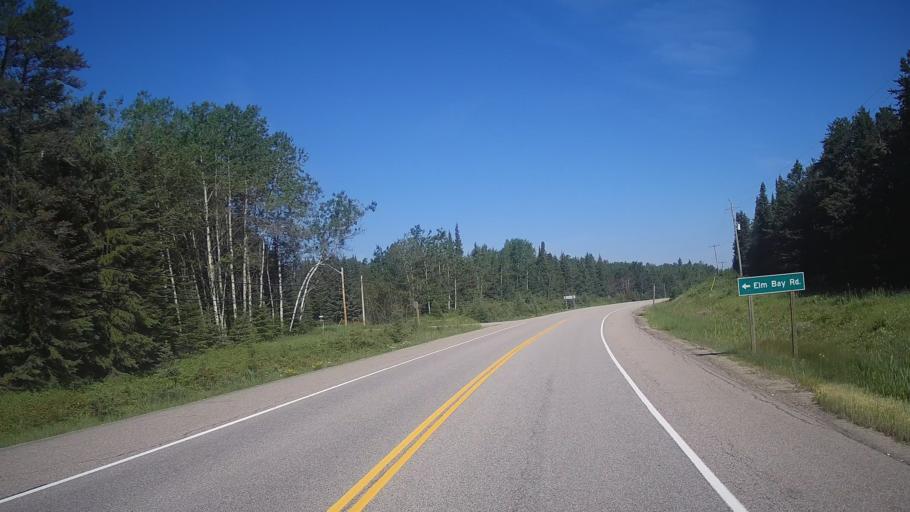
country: CA
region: Ontario
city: Dryden
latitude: 49.7681
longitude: -92.6870
